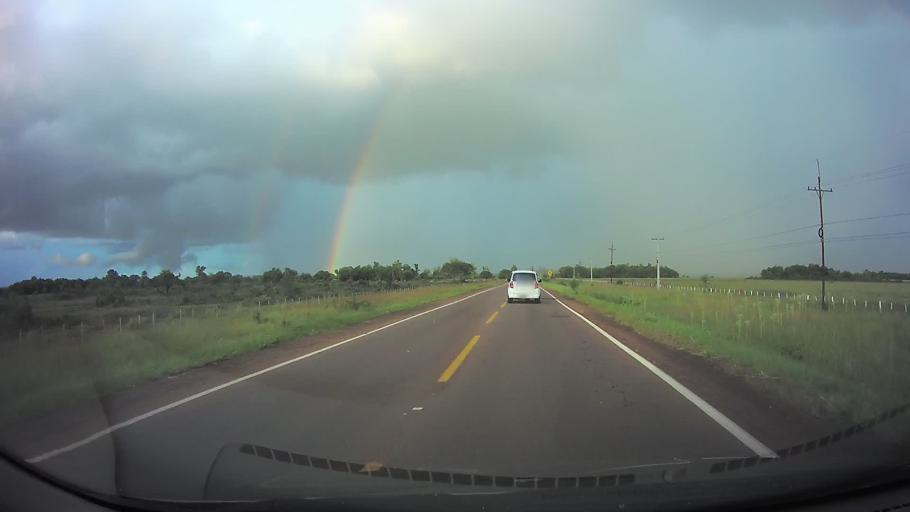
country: PY
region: Paraguari
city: Carapegua
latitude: -25.7141
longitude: -57.1935
